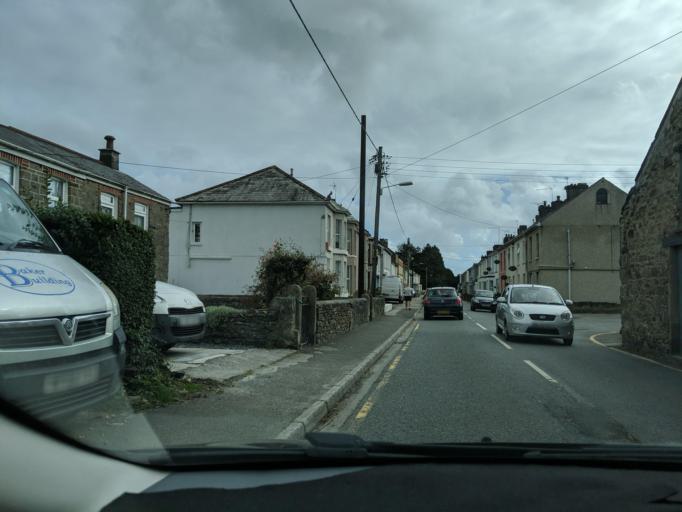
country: GB
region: England
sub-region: Cornwall
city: Par
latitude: 50.3593
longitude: -4.7140
